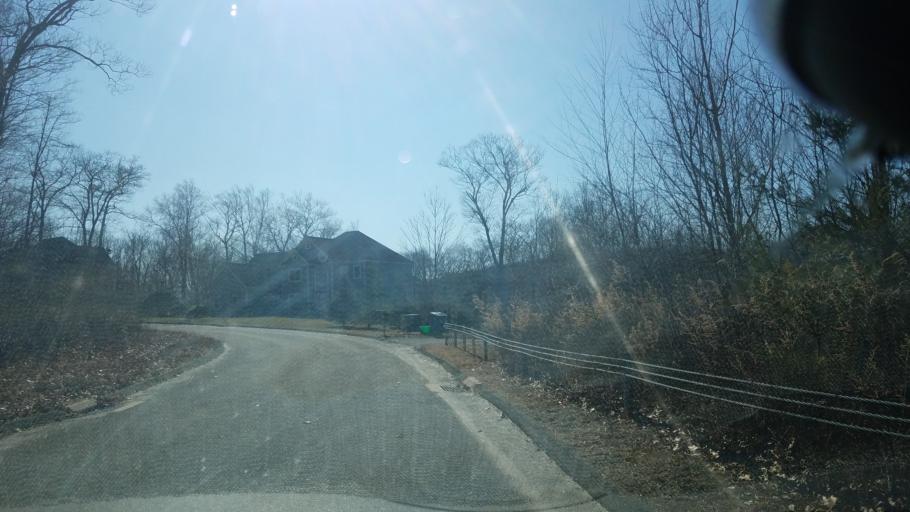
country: US
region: Connecticut
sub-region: Fairfield County
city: Newtown
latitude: 41.3865
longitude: -73.2473
